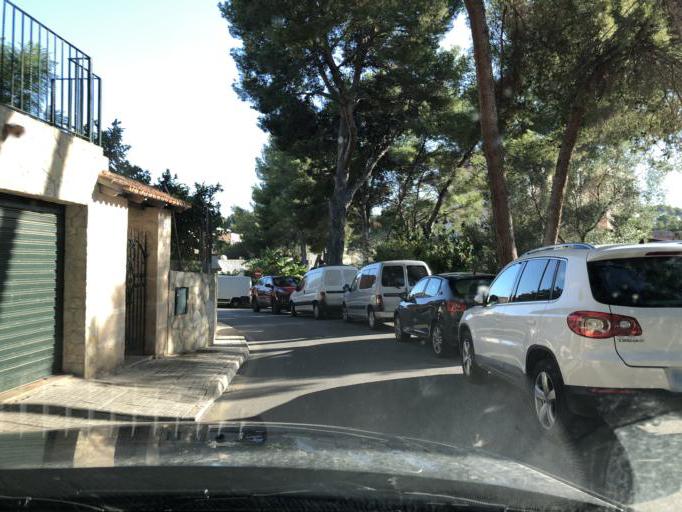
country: ES
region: Balearic Islands
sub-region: Illes Balears
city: Camp de Mar
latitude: 39.5391
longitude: 2.4447
